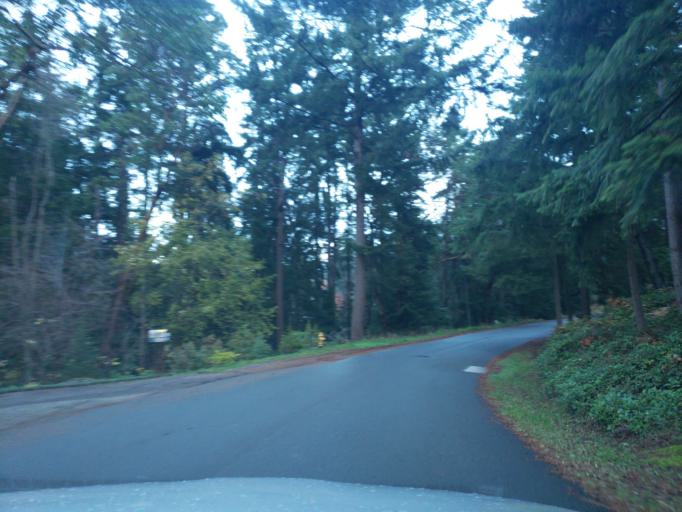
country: US
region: Washington
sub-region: Snohomish County
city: Woodway
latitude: 47.7664
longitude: -122.3802
